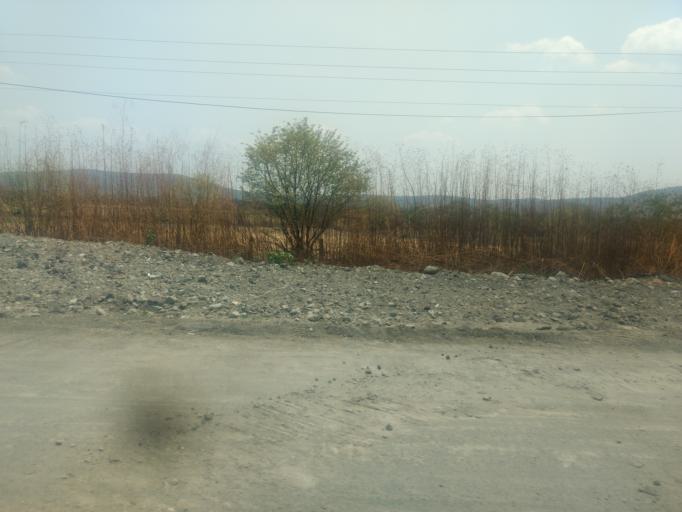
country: MX
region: Morelos
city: La Joya
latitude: 18.6756
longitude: -99.4362
